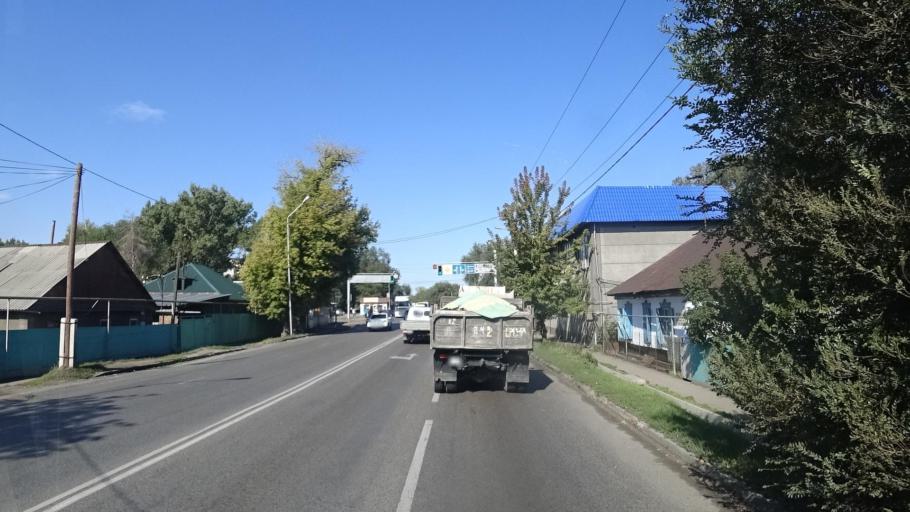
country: KZ
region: Almaty Oblysy
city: Pervomayskiy
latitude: 43.3544
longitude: 76.9500
